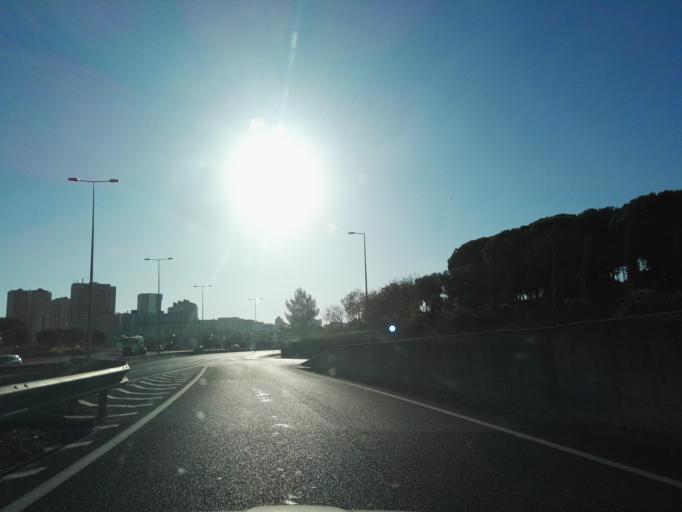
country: PT
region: Lisbon
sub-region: Lisbon
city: Lisbon
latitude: 38.7478
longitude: -9.1230
